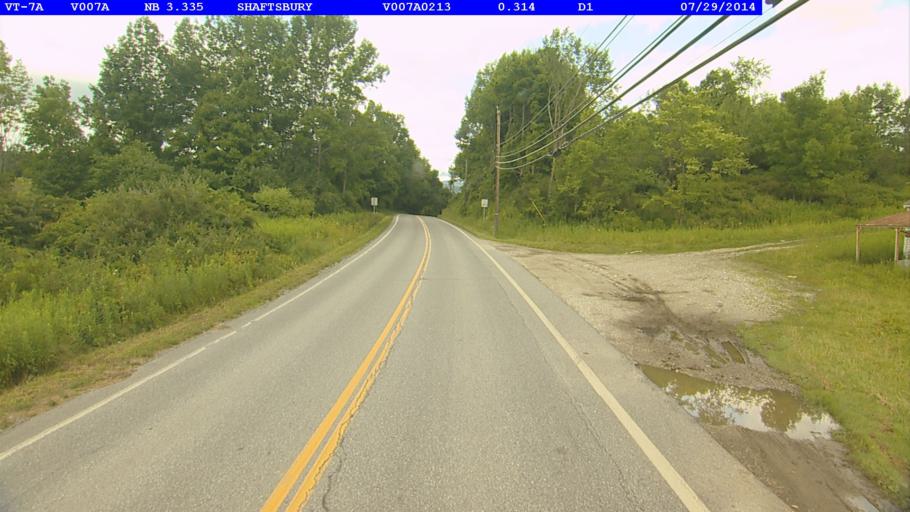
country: US
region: Vermont
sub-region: Bennington County
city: North Bennington
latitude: 42.9372
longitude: -73.2100
